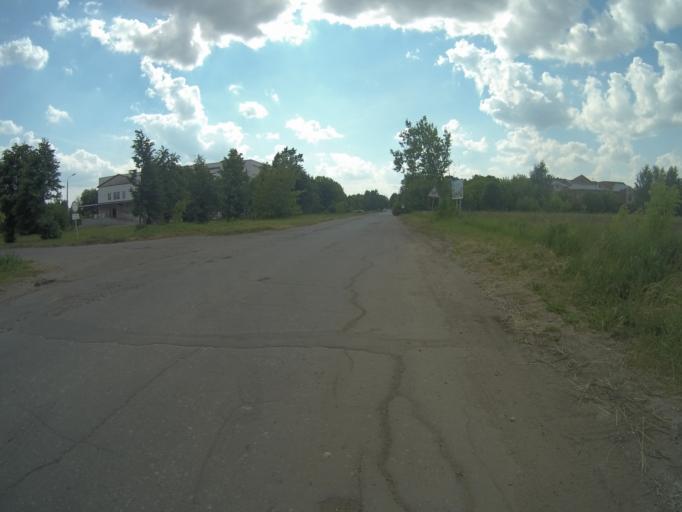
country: RU
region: Vladimir
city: Suzdal'
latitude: 56.4385
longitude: 40.4636
